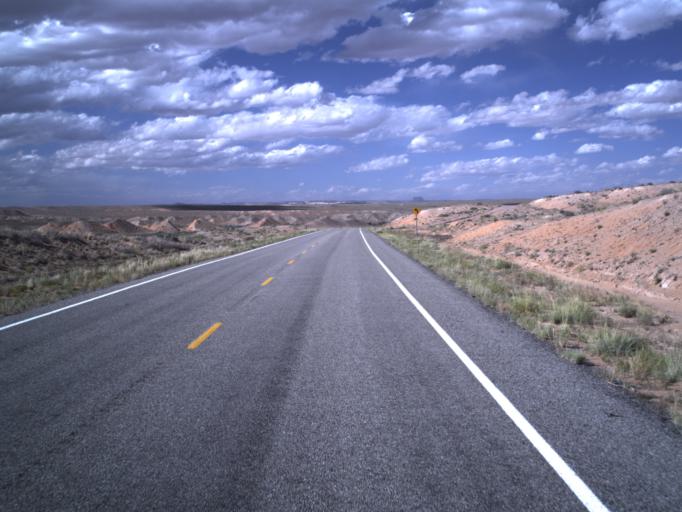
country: US
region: Utah
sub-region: Emery County
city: Ferron
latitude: 38.3164
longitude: -110.6738
